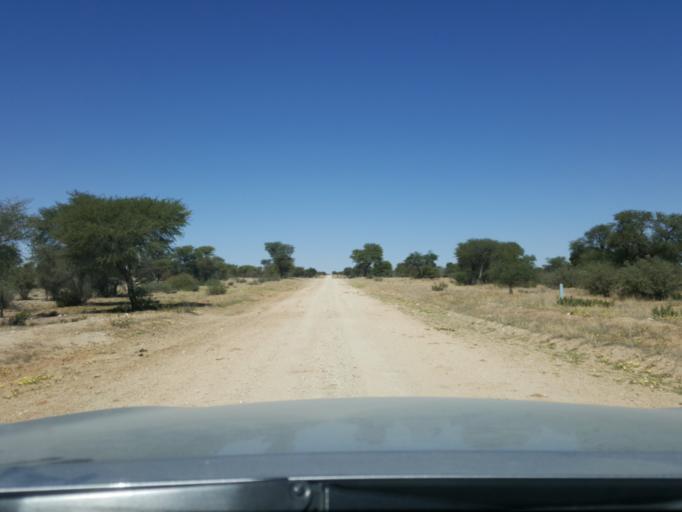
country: BW
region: Kgalagadi
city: Hukuntsi
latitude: -24.0641
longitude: 21.2234
